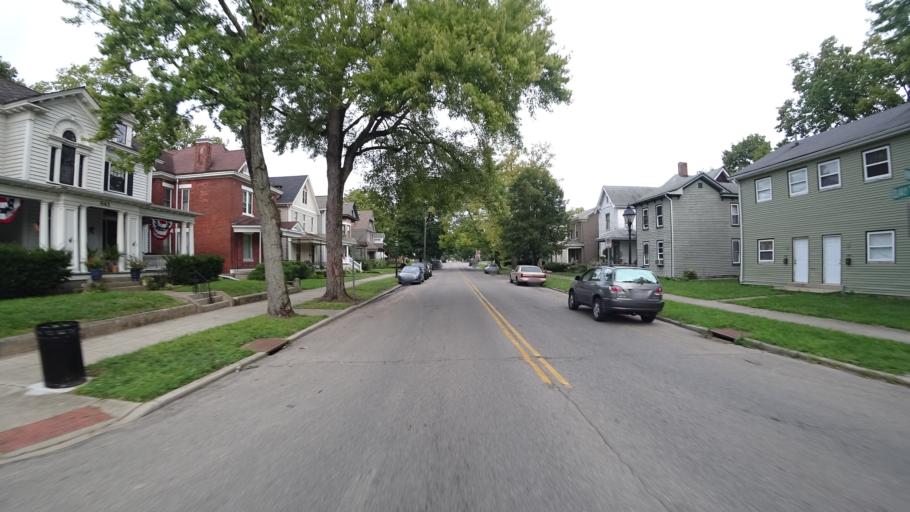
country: US
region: Ohio
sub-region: Butler County
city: Hamilton
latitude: 39.3992
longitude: -84.5507
